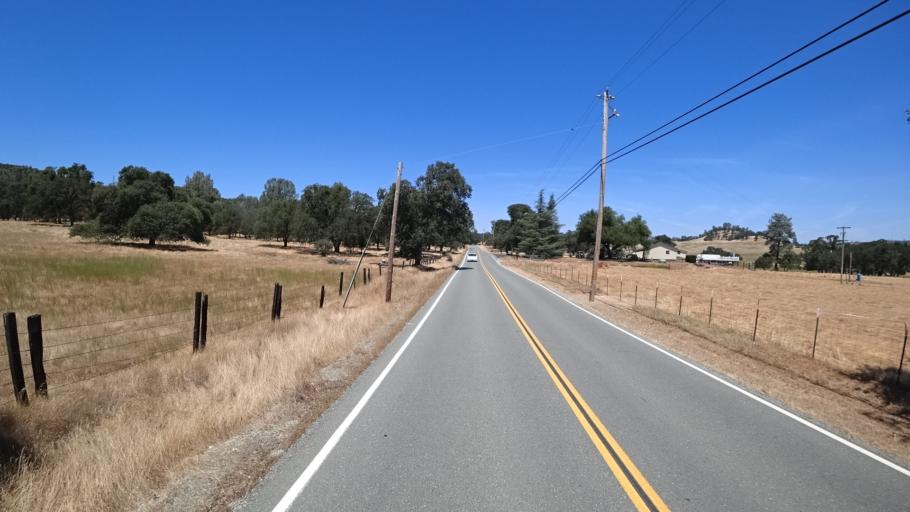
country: US
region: California
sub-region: Calaveras County
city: Valley Springs
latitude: 38.2134
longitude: -120.8323
